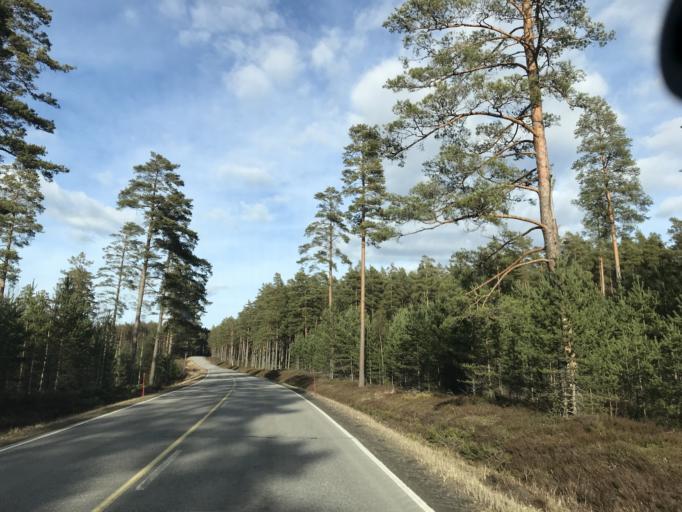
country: FI
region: Uusimaa
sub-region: Raaseporin
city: Ekenaes
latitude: 60.0686
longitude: 23.2851
